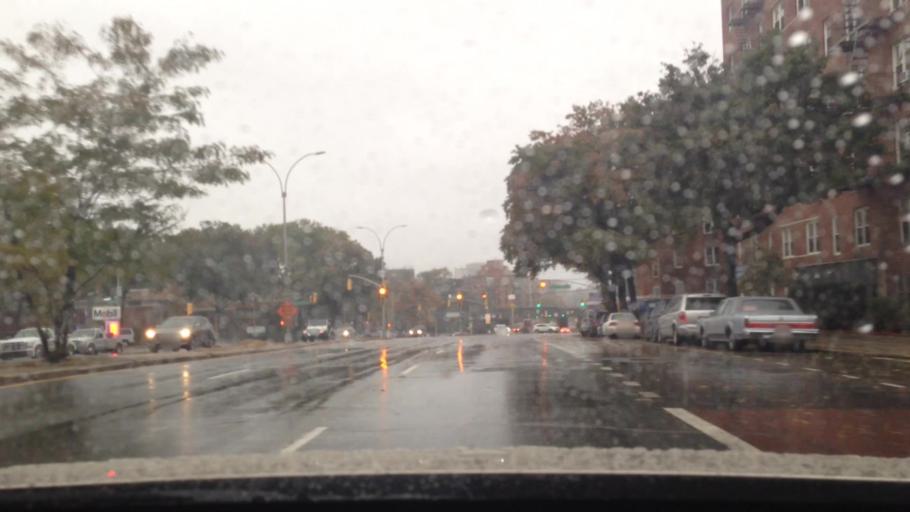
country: US
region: New York
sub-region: Queens County
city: Borough of Queens
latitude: 40.7269
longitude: -73.8704
